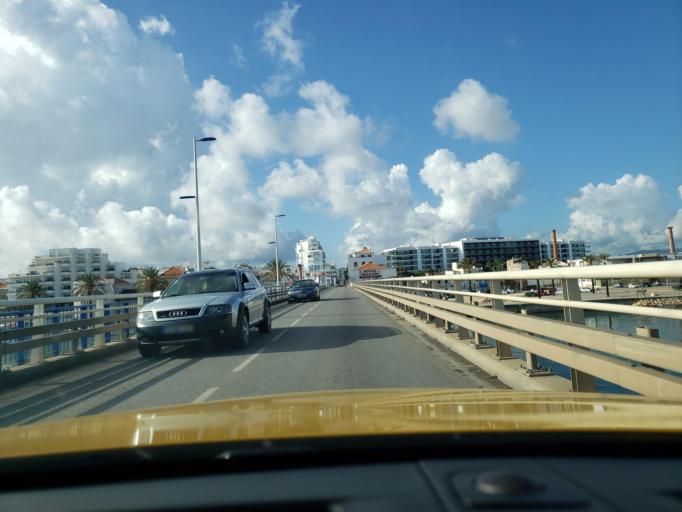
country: PT
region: Faro
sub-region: Portimao
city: Portimao
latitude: 37.1394
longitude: -8.5307
